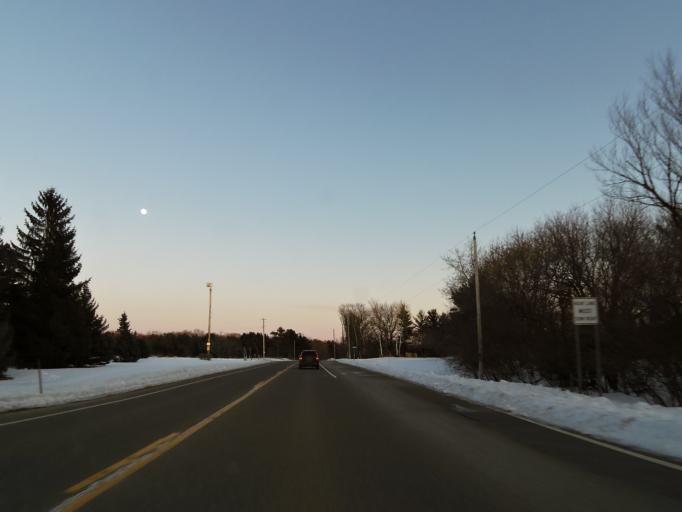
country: US
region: Minnesota
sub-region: Washington County
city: Grant
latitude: 45.0834
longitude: -92.9103
